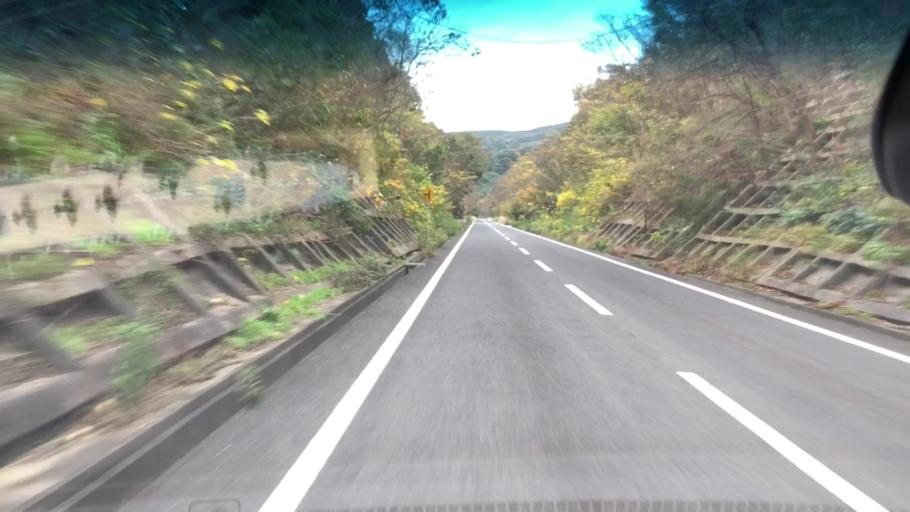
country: JP
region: Nagasaki
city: Sasebo
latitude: 33.0039
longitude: 129.7074
